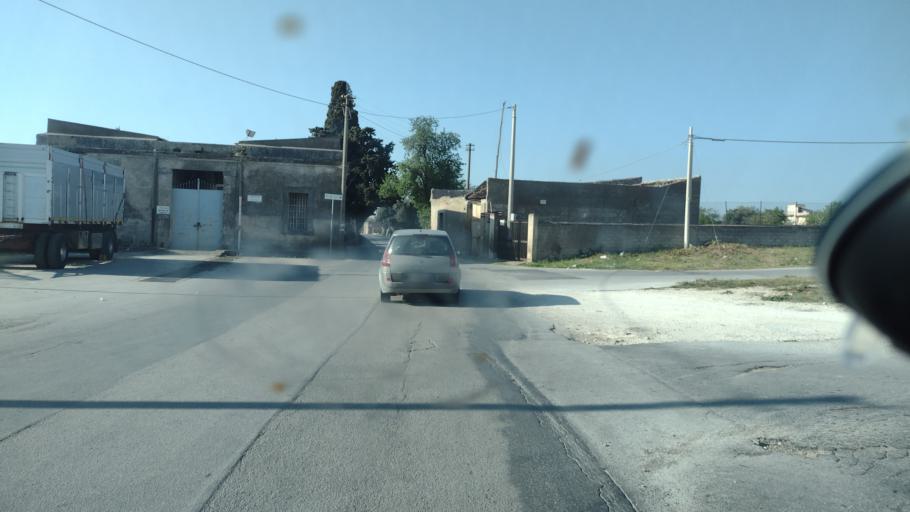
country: IT
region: Sicily
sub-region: Provincia di Siracusa
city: Avola
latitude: 36.9011
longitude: 15.1354
